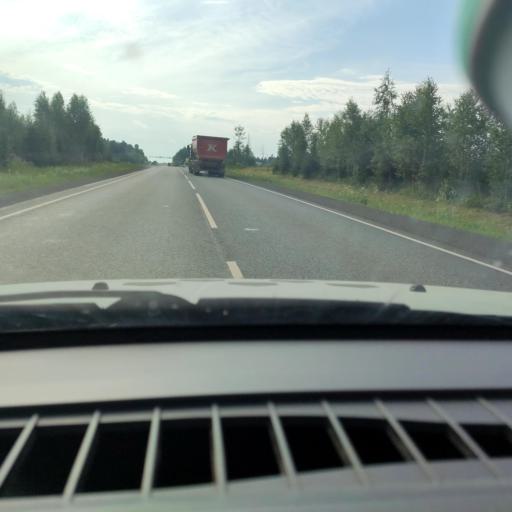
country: RU
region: Perm
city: Siva
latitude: 58.5134
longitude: 54.0217
